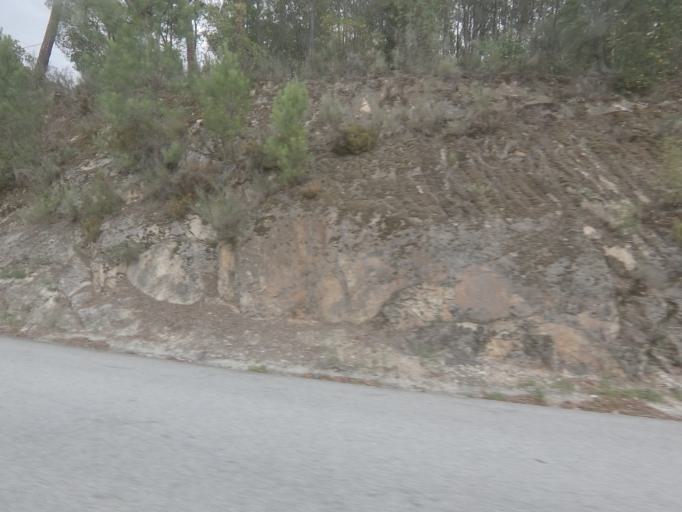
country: PT
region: Viseu
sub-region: Armamar
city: Armamar
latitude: 41.1119
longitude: -7.6756
